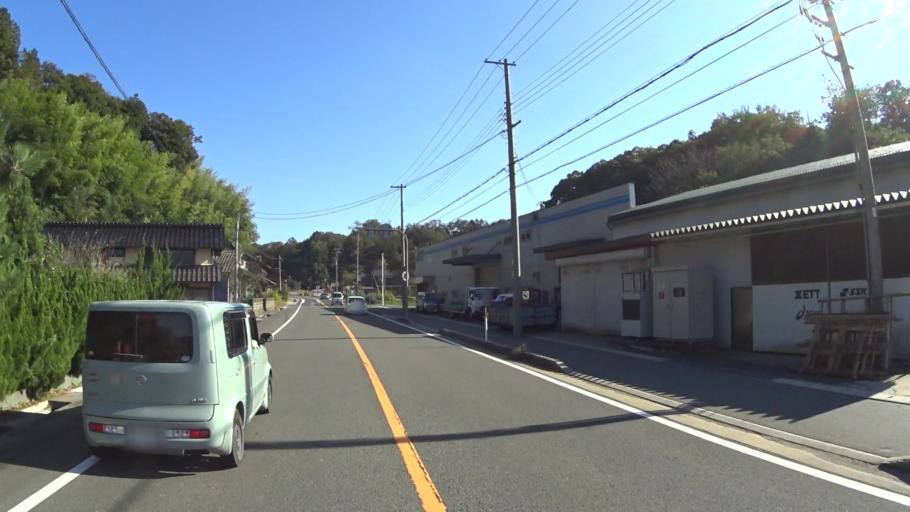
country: JP
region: Kyoto
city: Miyazu
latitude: 35.6477
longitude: 135.0436
